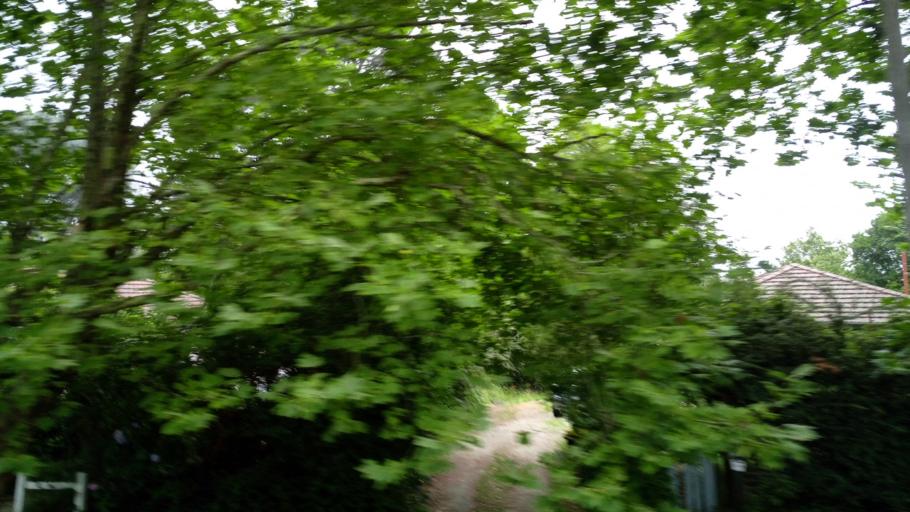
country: AU
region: New South Wales
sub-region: Blue Mountains Municipality
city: Leura
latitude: -33.7186
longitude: 150.3288
